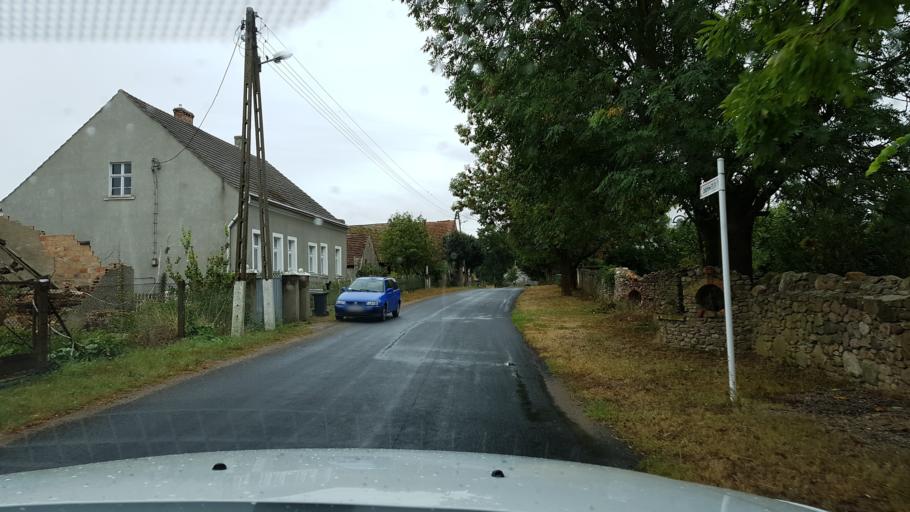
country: PL
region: West Pomeranian Voivodeship
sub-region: Powiat gryfinski
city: Cedynia
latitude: 52.8547
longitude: 14.2903
